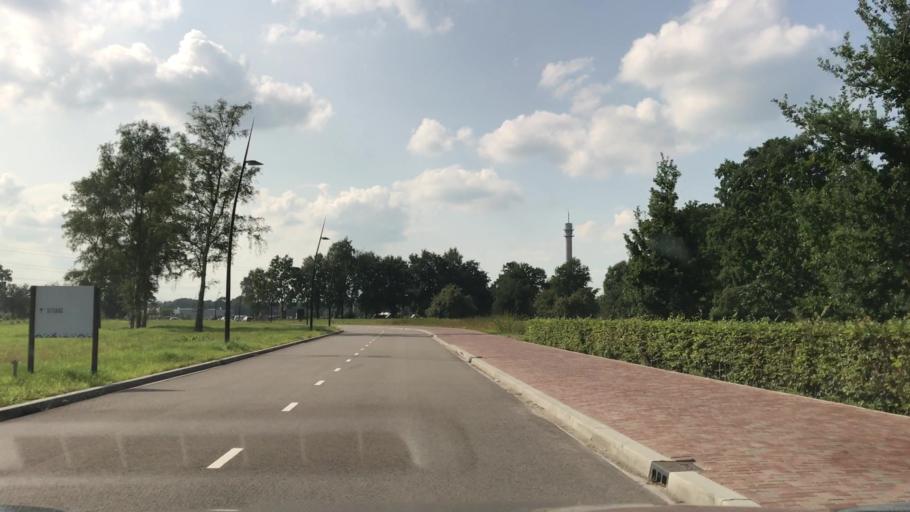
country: NL
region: Overijssel
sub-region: Gemeente Hengelo
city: Hengelo
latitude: 52.2464
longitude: 6.7687
